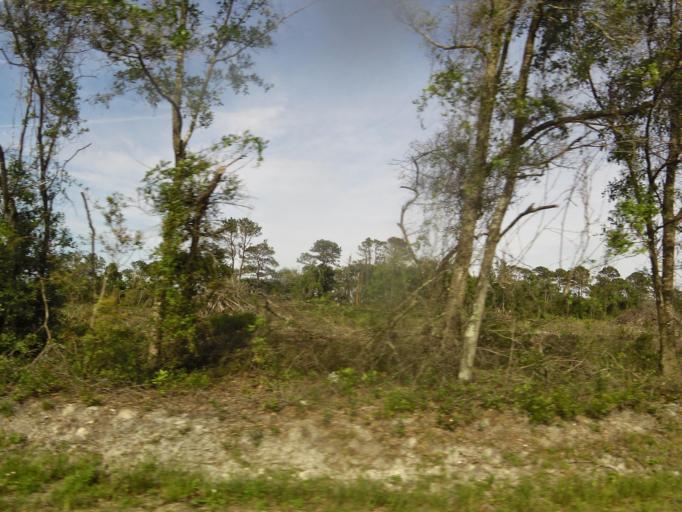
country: US
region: Florida
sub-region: Nassau County
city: Fernandina Beach
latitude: 30.4986
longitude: -81.4722
